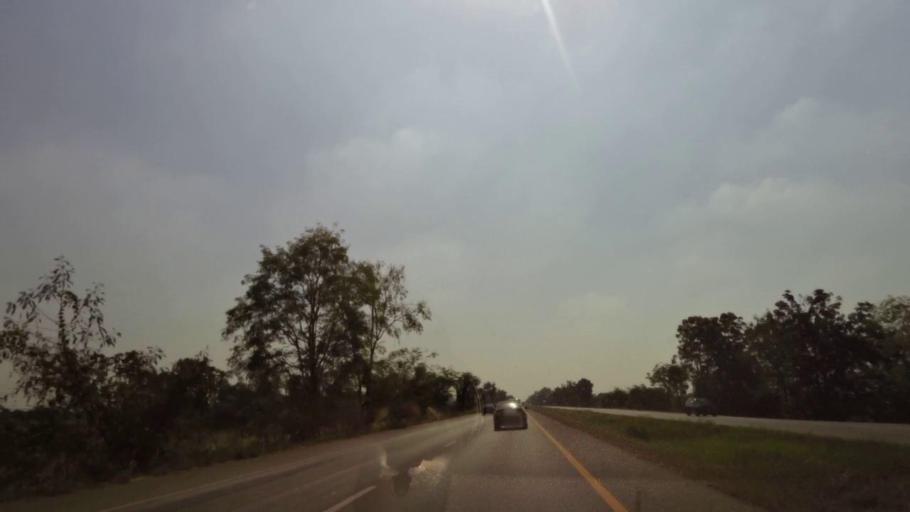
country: TH
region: Phichit
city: Wachira Barami
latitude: 16.4511
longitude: 100.1465
